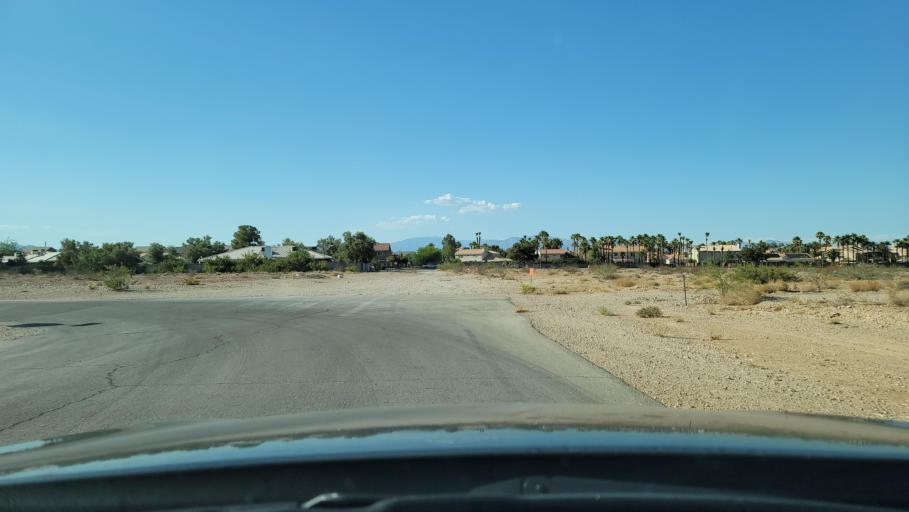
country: US
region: Nevada
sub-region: Clark County
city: Spring Valley
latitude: 36.0832
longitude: -115.2318
